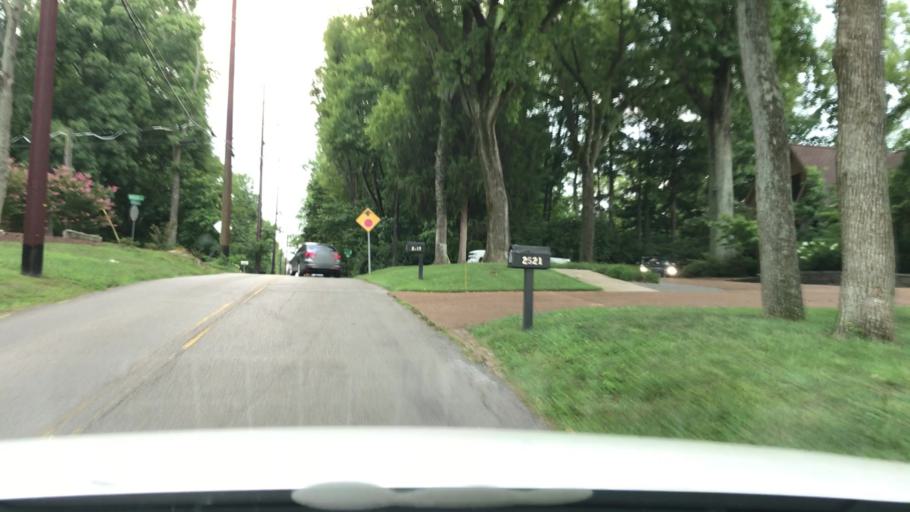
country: US
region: Tennessee
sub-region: Davidson County
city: Belle Meade
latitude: 36.1257
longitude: -86.8171
